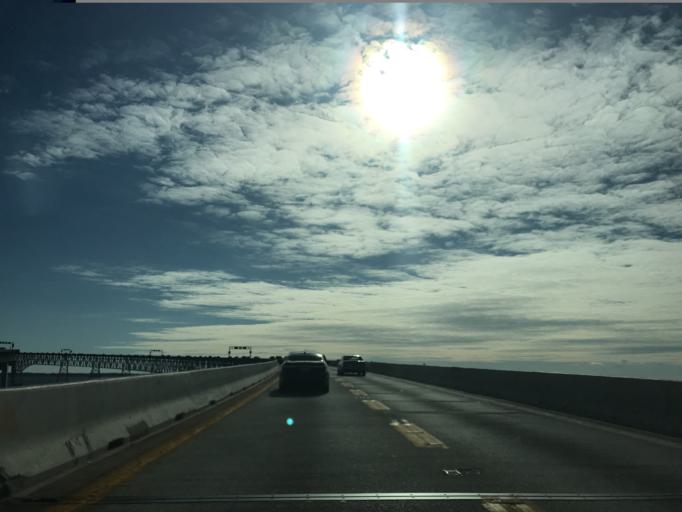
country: US
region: Maryland
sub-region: Anne Arundel County
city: Cape Saint Claire
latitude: 39.0005
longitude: -76.3994
